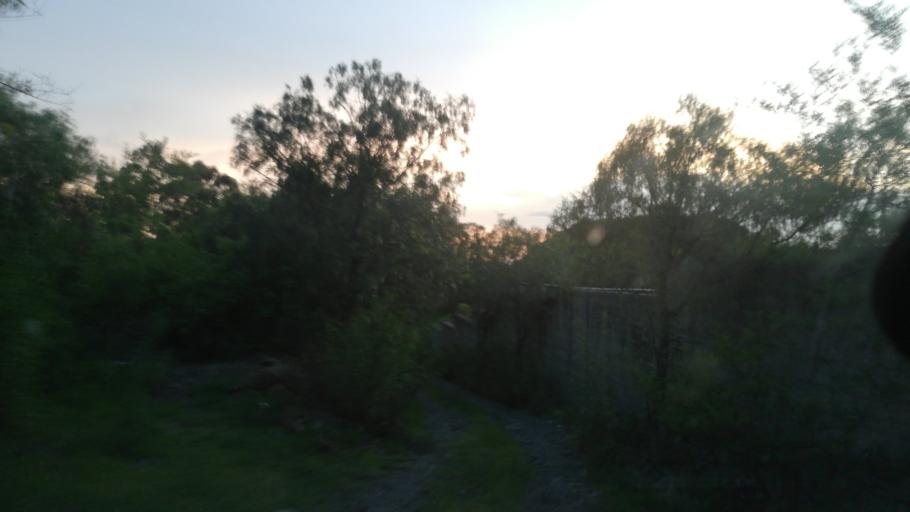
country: BO
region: Cochabamba
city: Cochabamba
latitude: -17.3275
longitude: -66.2073
